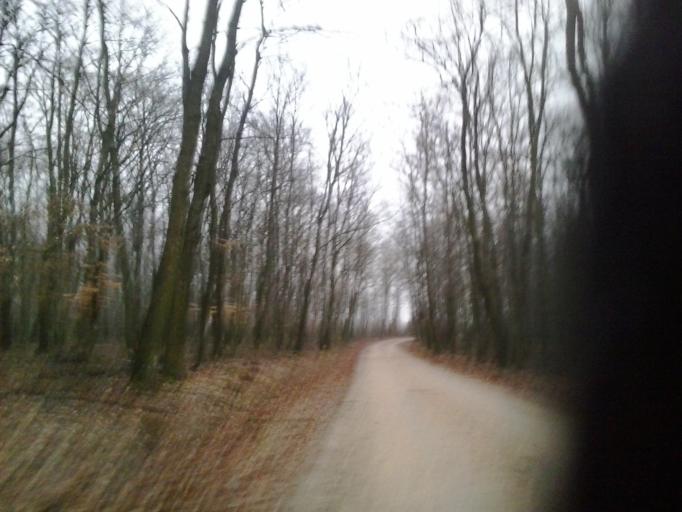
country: HU
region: Vas
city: Sarvar
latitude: 47.1428
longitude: 16.9756
